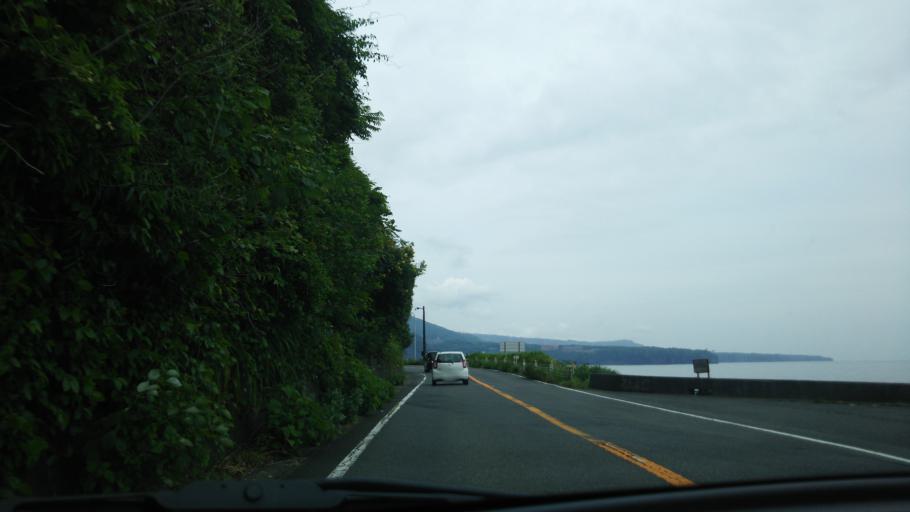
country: JP
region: Shizuoka
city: Ito
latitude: 34.8373
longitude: 139.0774
